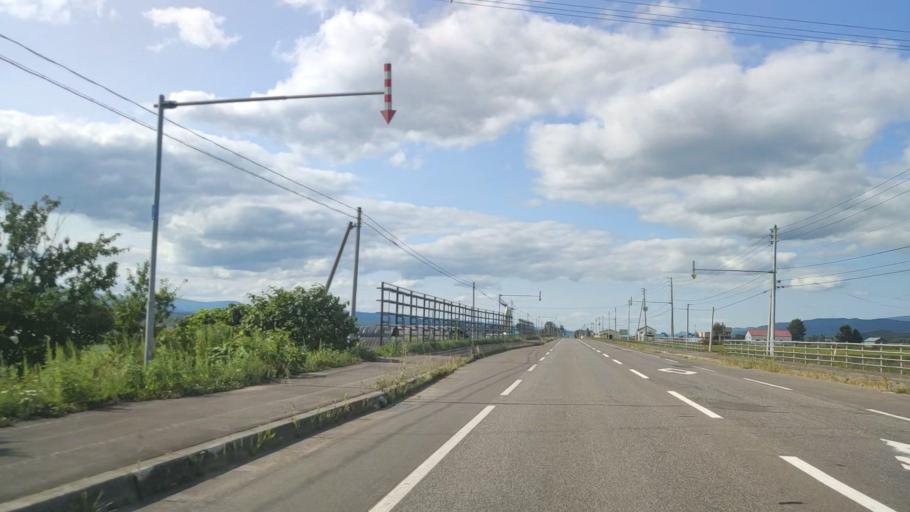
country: JP
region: Hokkaido
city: Nayoro
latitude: 44.4607
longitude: 142.3566
